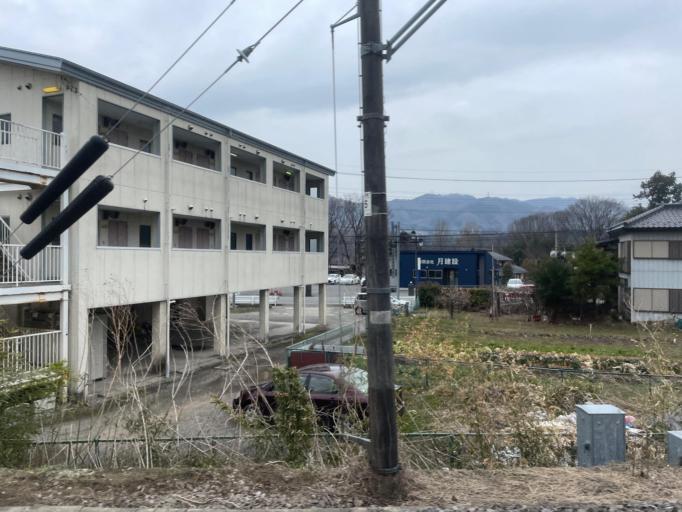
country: JP
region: Gunma
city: Numata
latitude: 36.6765
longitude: 139.0042
